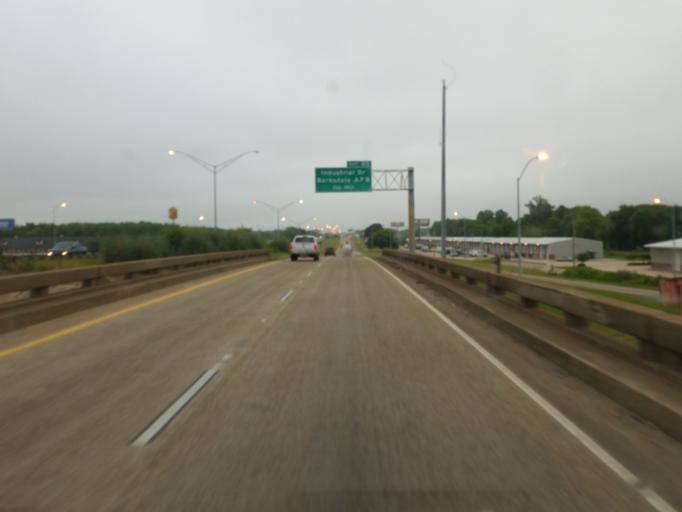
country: US
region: Louisiana
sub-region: Bossier Parish
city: Bossier City
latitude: 32.5254
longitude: -93.6994
